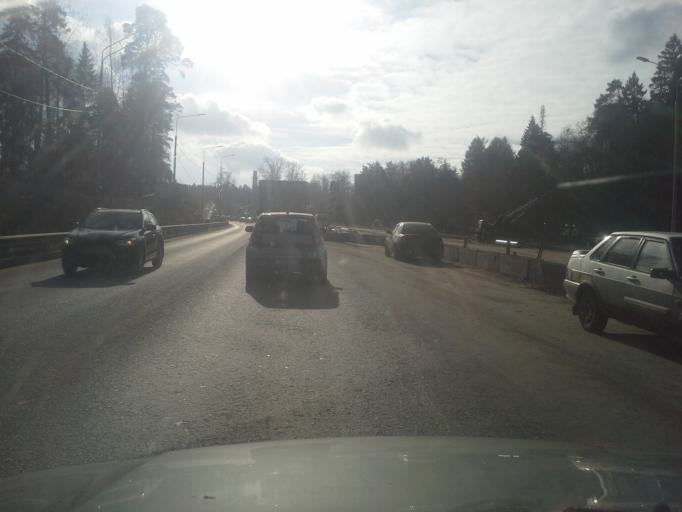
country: RU
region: Moskovskaya
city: Zvenigorod
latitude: 55.7095
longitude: 36.8742
